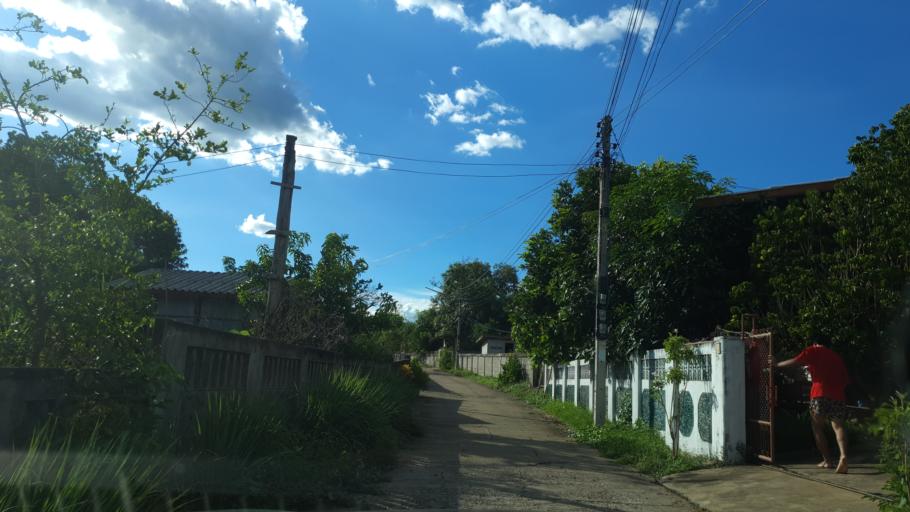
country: TH
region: Lampang
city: Sop Prap
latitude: 17.8793
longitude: 99.2964
